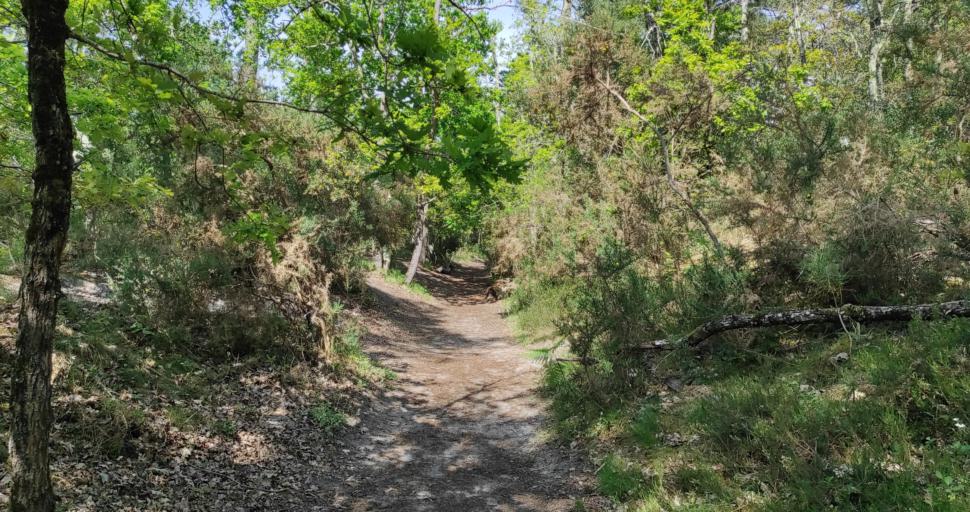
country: FR
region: Aquitaine
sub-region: Departement de la Gironde
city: Andernos-les-Bains
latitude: 44.7537
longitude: -1.1176
